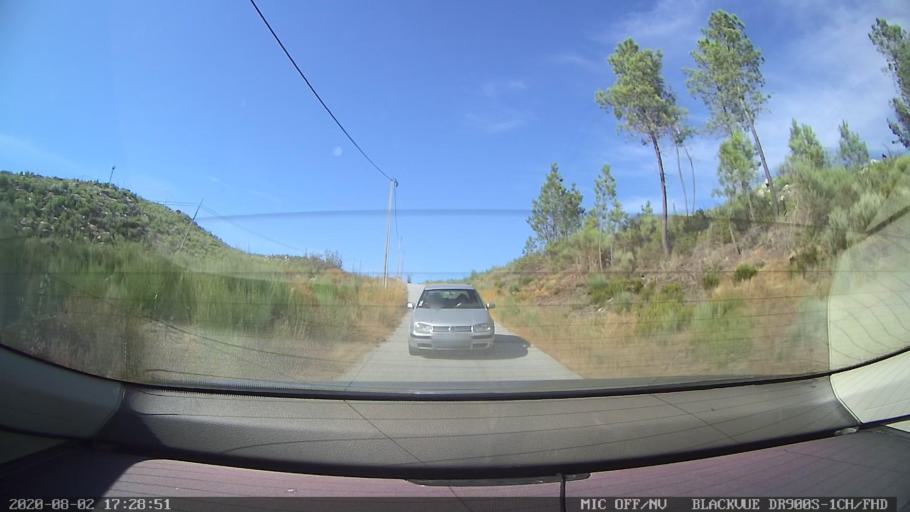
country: PT
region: Vila Real
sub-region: Sabrosa
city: Sabrosa
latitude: 41.3547
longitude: -7.5903
